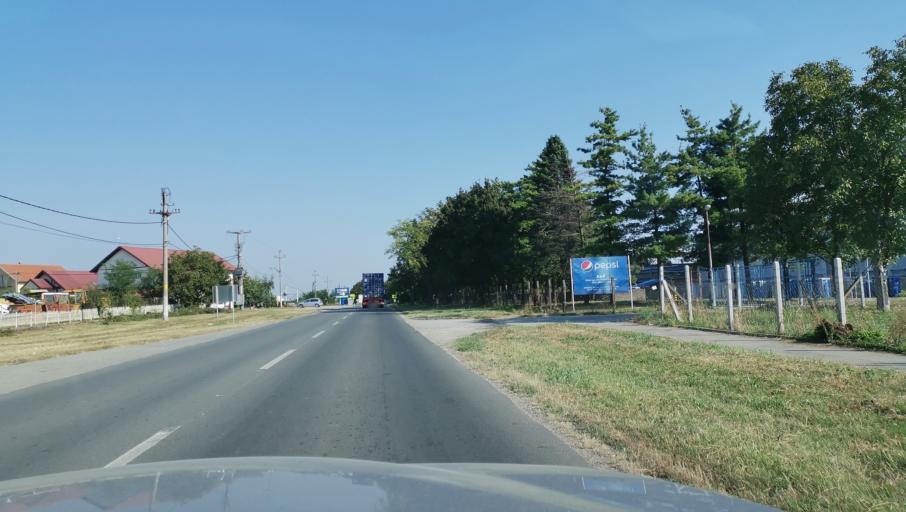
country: RS
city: Dobanovci
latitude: 44.8126
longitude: 20.2407
